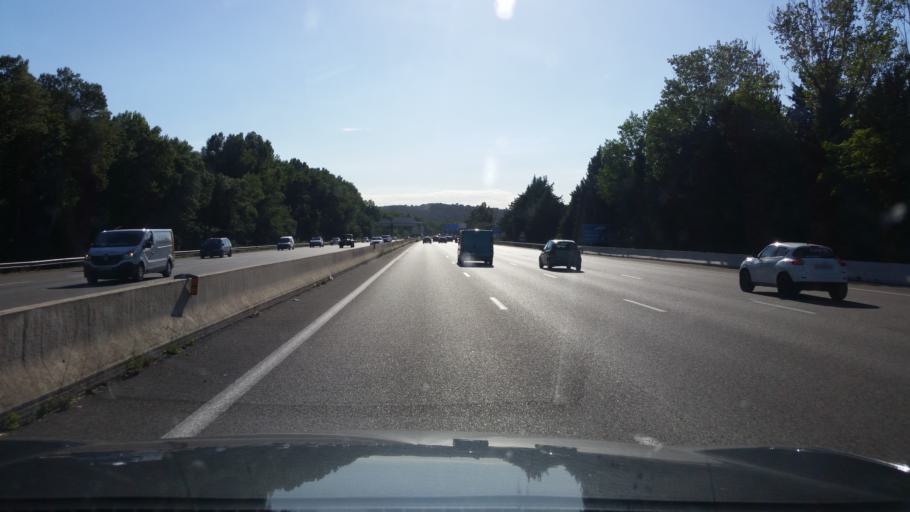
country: FR
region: Provence-Alpes-Cote d'Azur
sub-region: Departement des Bouches-du-Rhone
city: Chateauneuf-le-Rouge
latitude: 43.4817
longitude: 5.5532
